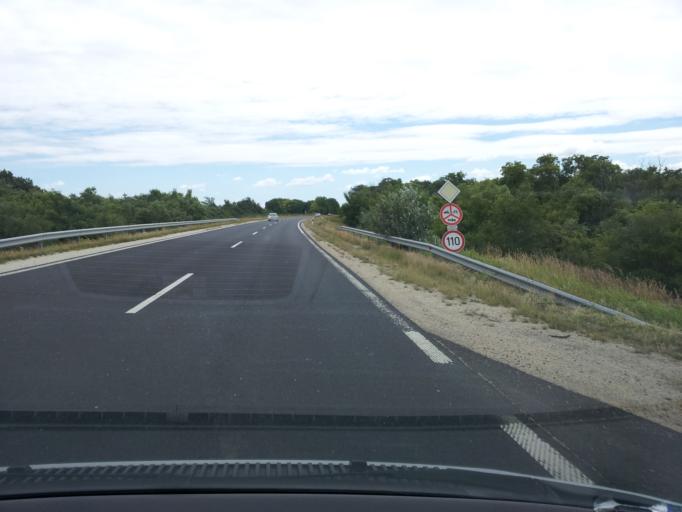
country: HU
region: Veszprem
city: Balatonkenese
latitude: 47.0588
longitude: 18.1248
